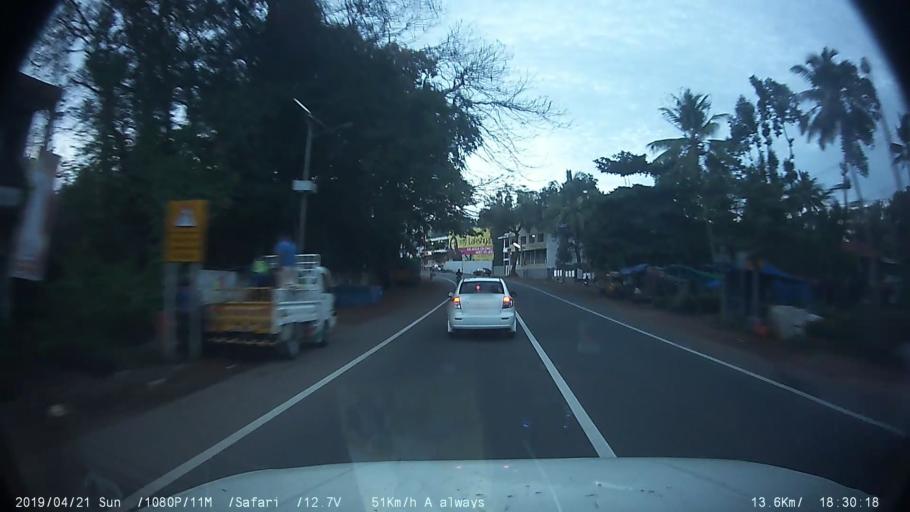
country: IN
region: Kerala
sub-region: Kottayam
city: Changanacheri
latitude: 9.5130
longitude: 76.5277
